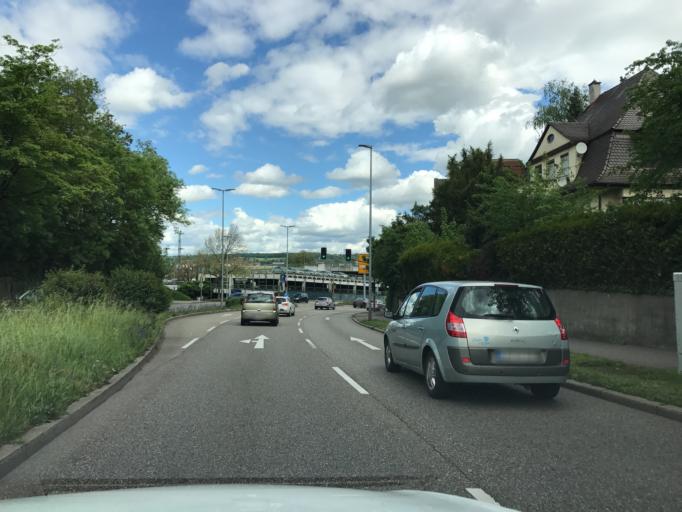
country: DE
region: Baden-Wuerttemberg
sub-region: Regierungsbezirk Stuttgart
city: Bietigheim-Bissingen
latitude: 48.9464
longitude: 9.1387
